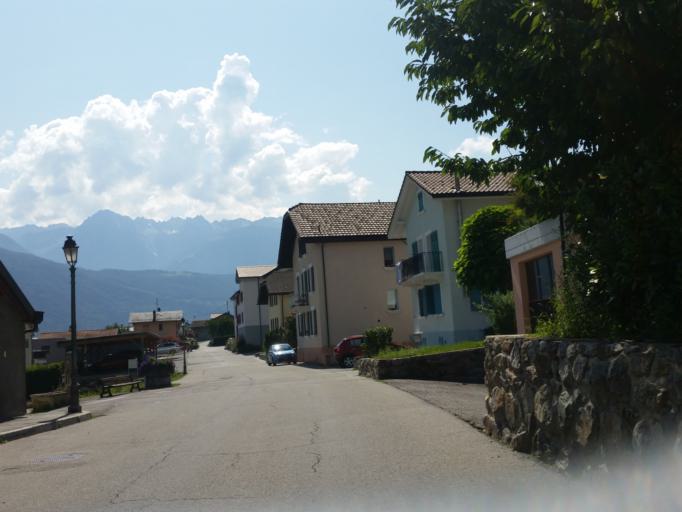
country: CH
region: Valais
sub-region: Martigny District
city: Fully
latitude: 46.1363
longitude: 7.1089
